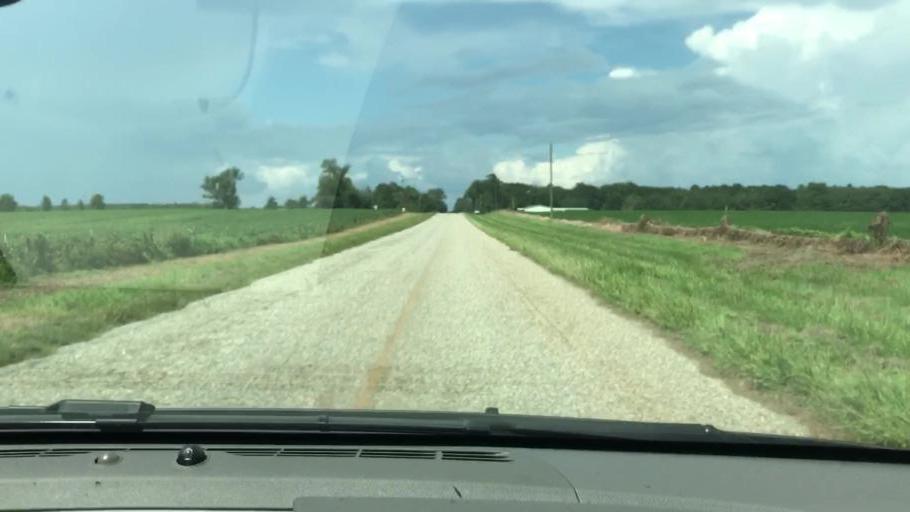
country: US
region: Georgia
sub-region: Early County
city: Blakely
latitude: 31.2000
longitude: -85.0037
